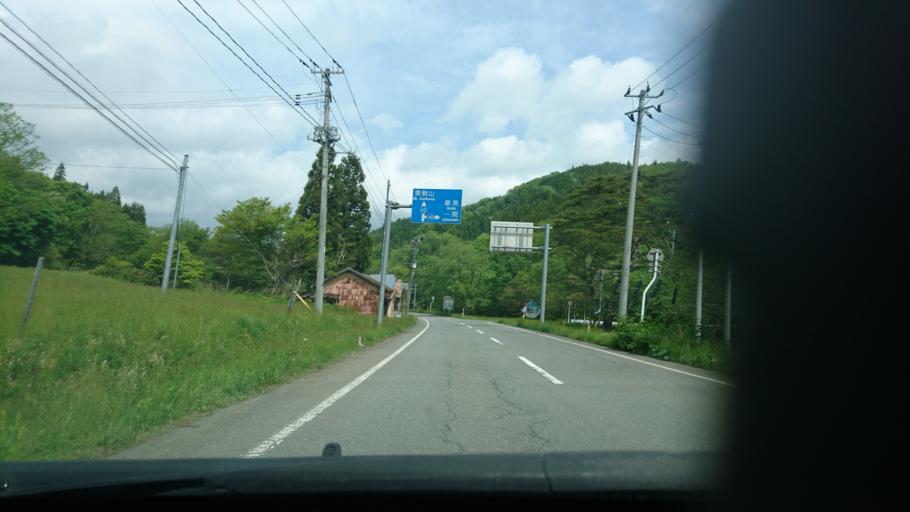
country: JP
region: Iwate
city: Ichinoseki
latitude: 38.9060
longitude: 140.8983
